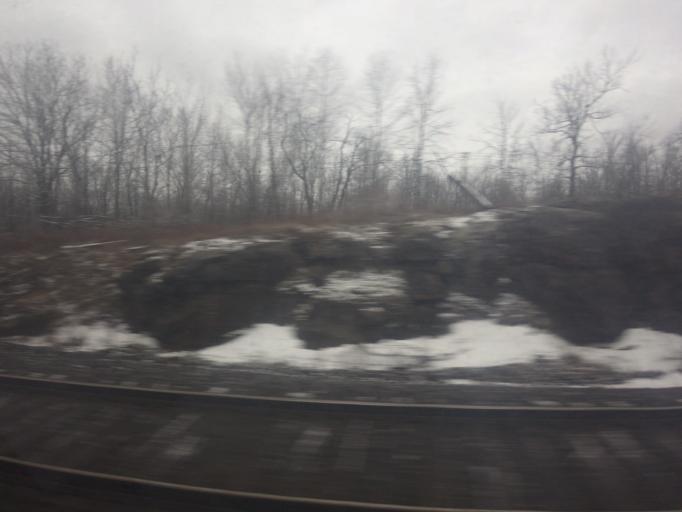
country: CA
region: Ontario
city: Gananoque
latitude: 44.3590
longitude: -76.2040
